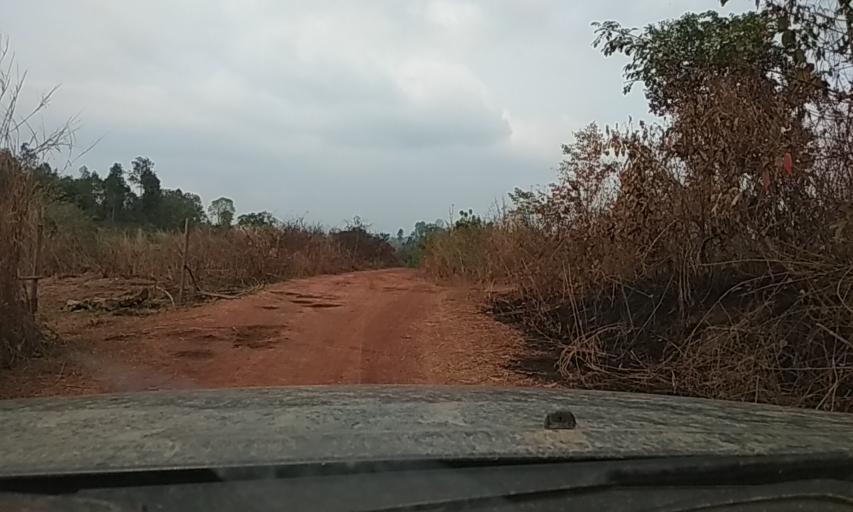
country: TH
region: Nan
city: Mae Charim
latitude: 18.4360
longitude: 101.1837
